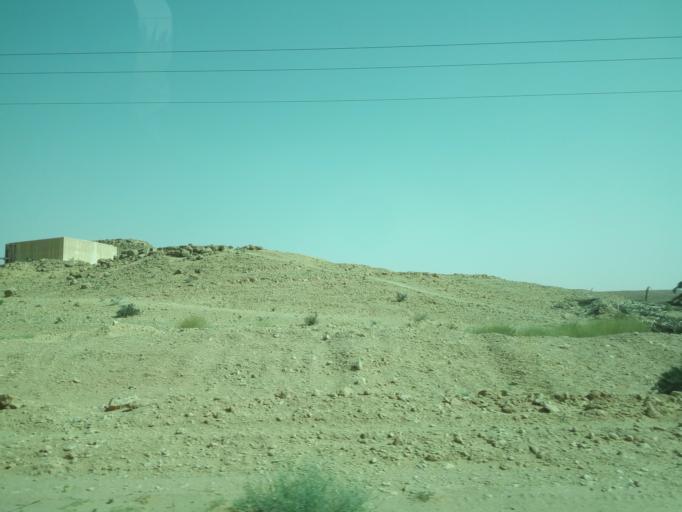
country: DZ
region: Ghardaia
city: Berriane
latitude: 32.8475
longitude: 3.9167
